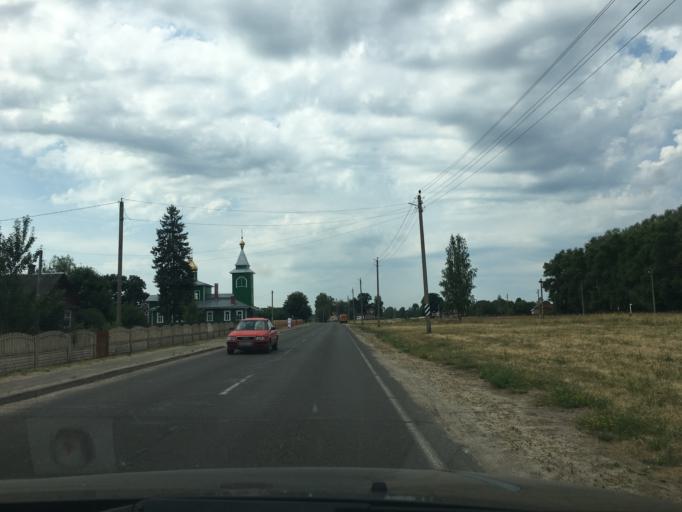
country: LT
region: Alytaus apskritis
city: Druskininkai
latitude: 53.8901
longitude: 24.1396
